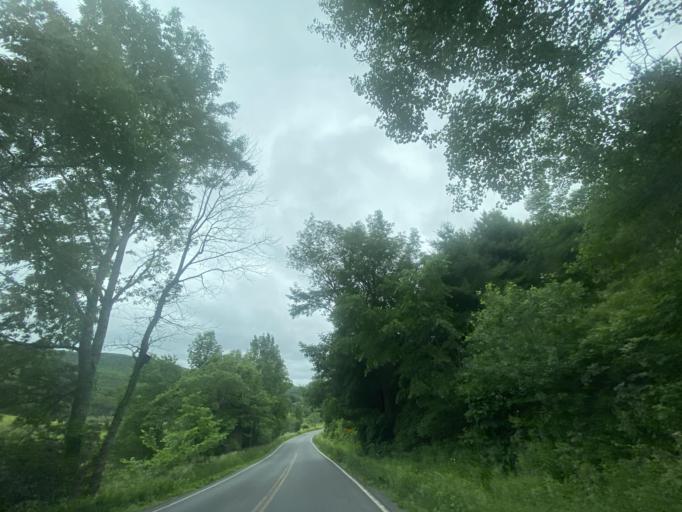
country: US
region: New York
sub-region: Schoharie County
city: Middleburgh
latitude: 42.3863
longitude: -74.3537
